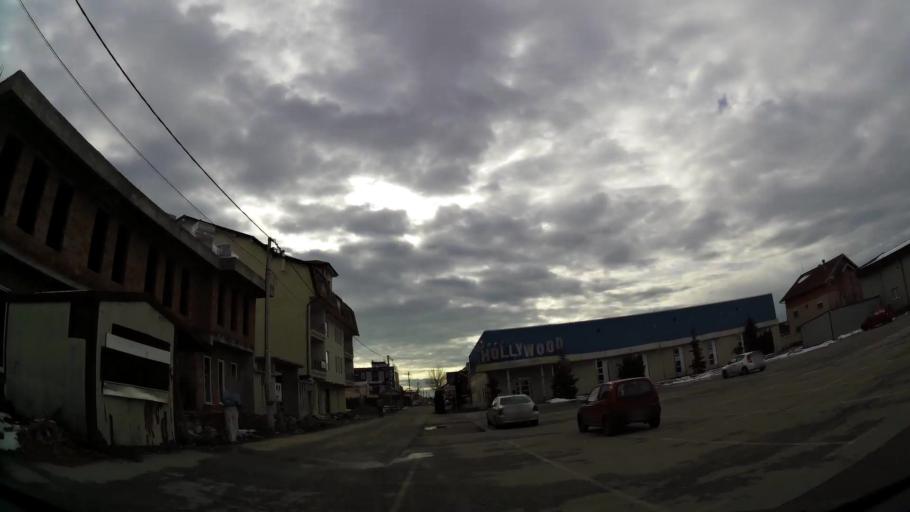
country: RS
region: Central Serbia
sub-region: Belgrade
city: Surcin
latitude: 44.8025
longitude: 20.3423
